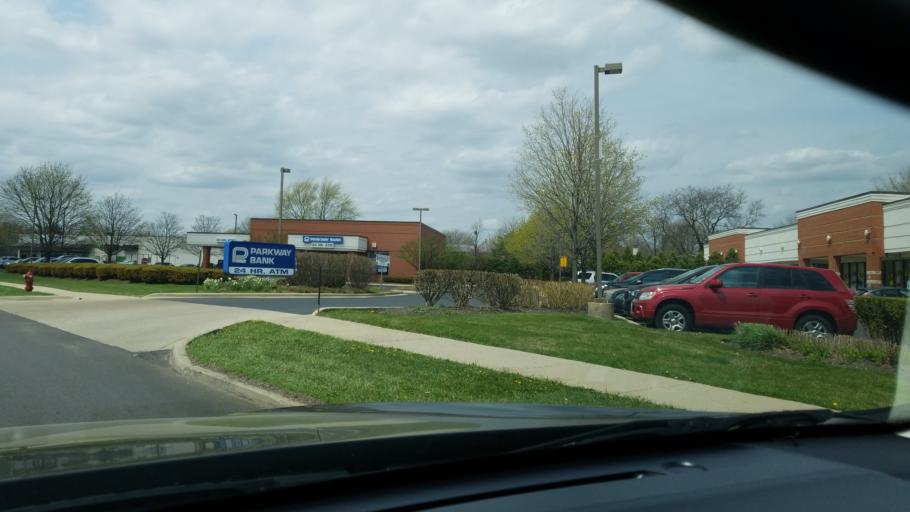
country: US
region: Illinois
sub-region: Cook County
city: Rolling Meadows
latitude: 42.0560
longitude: -88.0001
